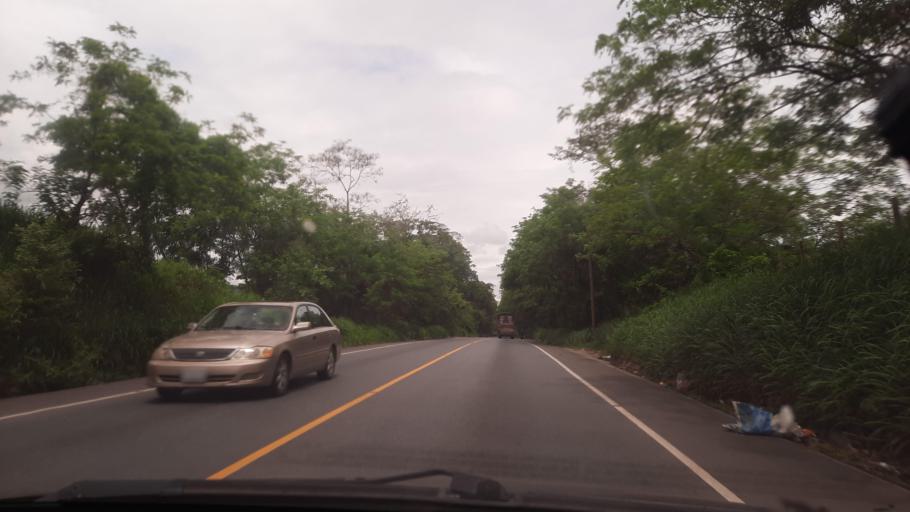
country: GT
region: Izabal
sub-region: Municipio de Los Amates
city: Los Amates
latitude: 15.2203
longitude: -89.2216
